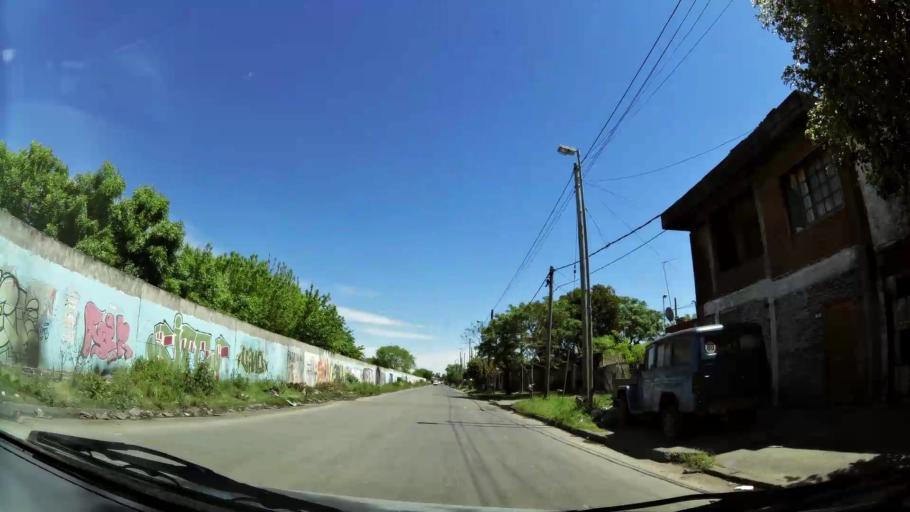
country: AR
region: Buenos Aires
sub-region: Partido de Lanus
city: Lanus
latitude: -34.7321
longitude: -58.3392
